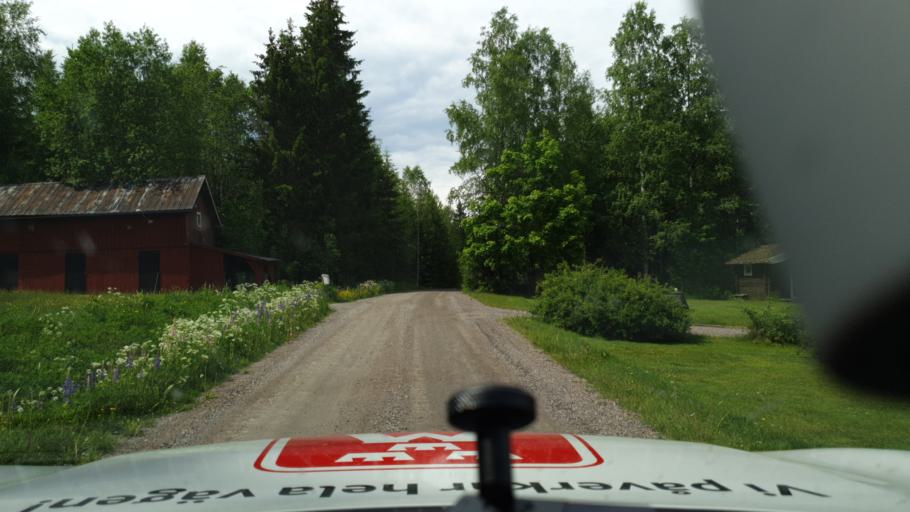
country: SE
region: Vaermland
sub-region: Torsby Kommun
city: Torsby
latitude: 59.9823
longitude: 12.8351
